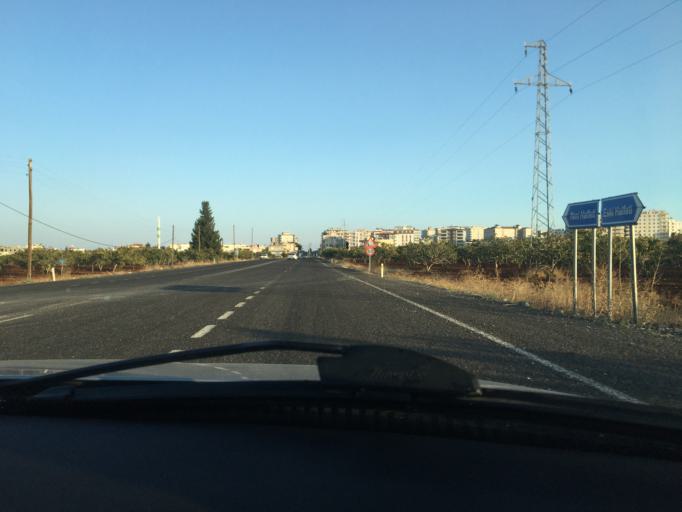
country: TR
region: Sanliurfa
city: Halfeti
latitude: 37.2334
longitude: 37.9370
